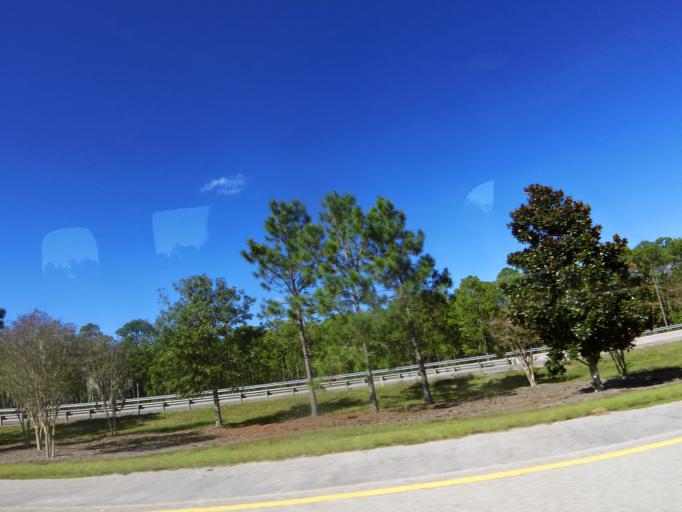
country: US
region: Florida
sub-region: Saint Johns County
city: Palm Valley
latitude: 30.1148
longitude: -81.4324
